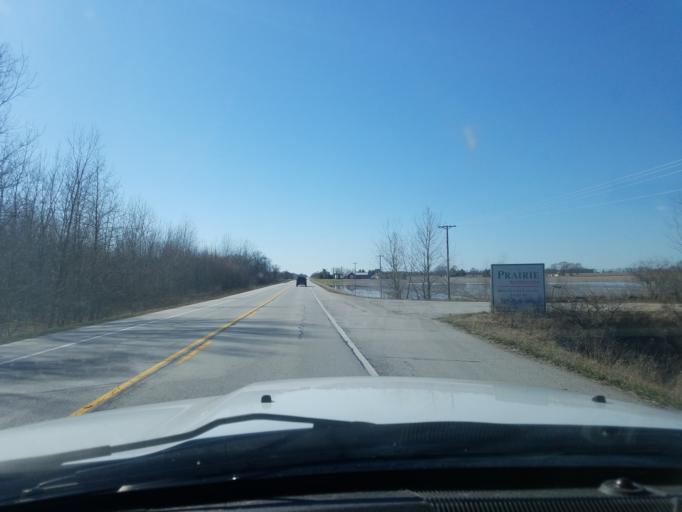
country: US
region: Indiana
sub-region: Shelby County
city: Shelbyville
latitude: 39.4964
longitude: -85.8686
